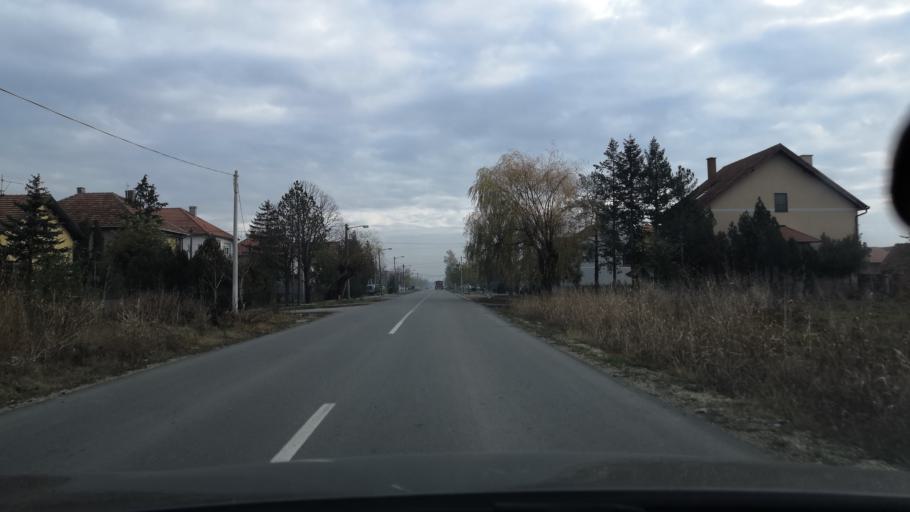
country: RS
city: Ugrinovci
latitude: 44.8798
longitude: 20.1680
